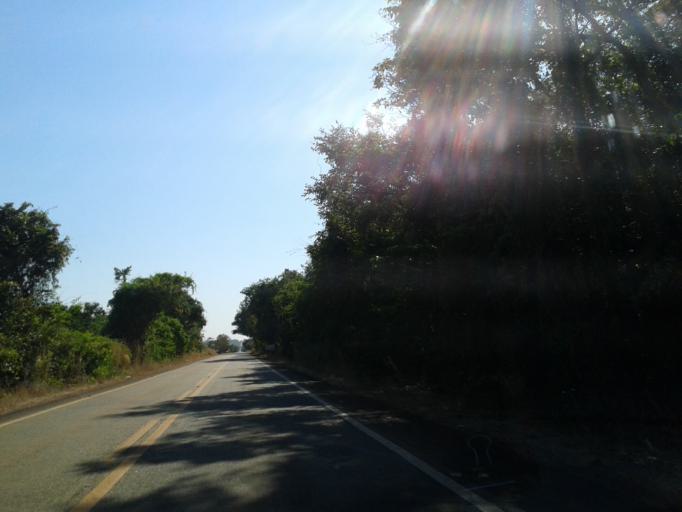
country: BR
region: Goias
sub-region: Mozarlandia
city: Mozarlandia
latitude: -14.5948
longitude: -50.5095
